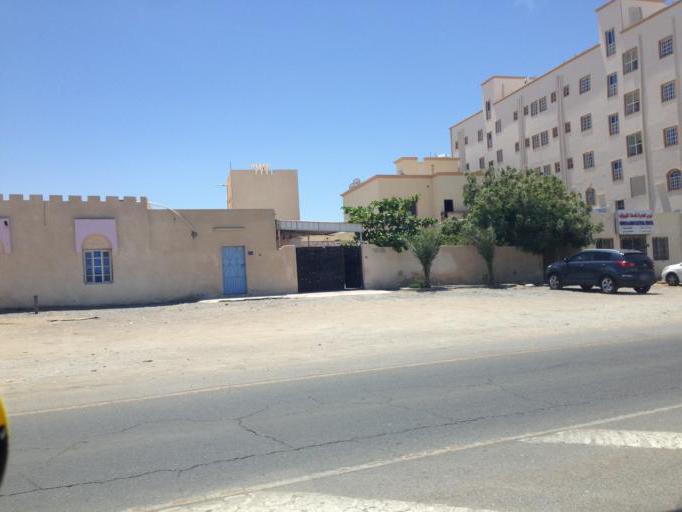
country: OM
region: Muhafazat Masqat
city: As Sib al Jadidah
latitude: 23.6427
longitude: 58.2378
